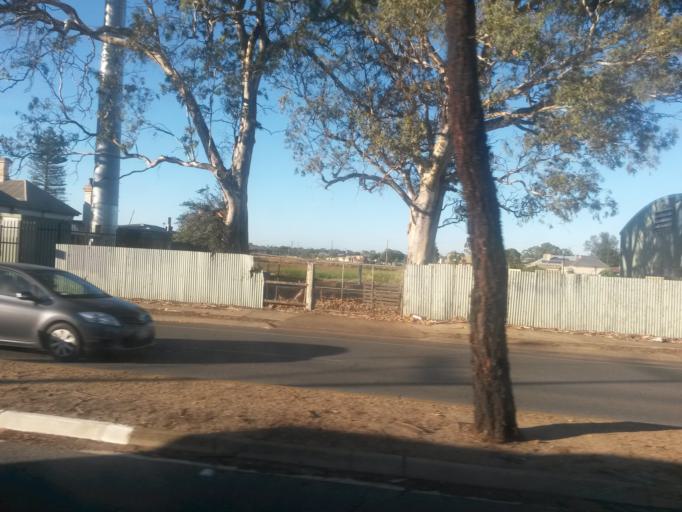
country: AU
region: South Australia
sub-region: Port Adelaide Enfield
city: Alberton
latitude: -34.8644
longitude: 138.5306
